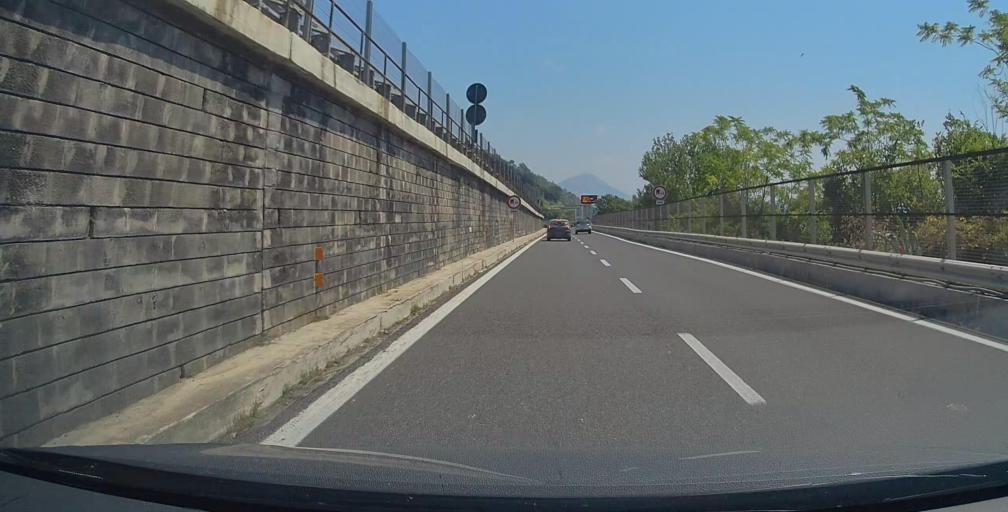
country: IT
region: Campania
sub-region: Provincia di Salerno
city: Vietri sul Mare
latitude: 40.6796
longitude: 14.7432
